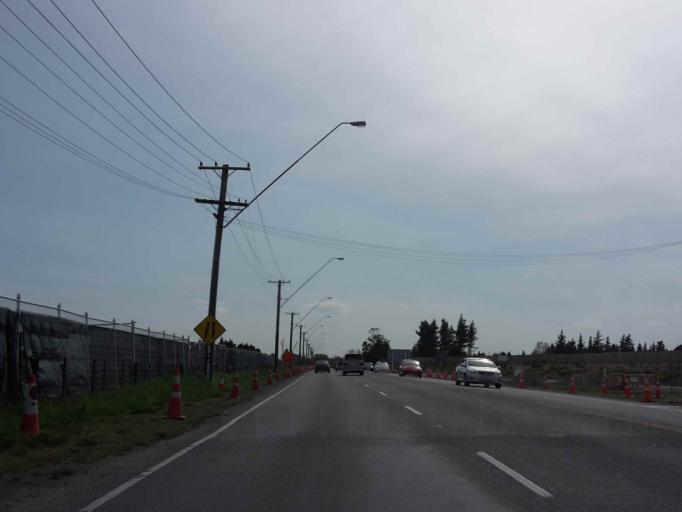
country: NZ
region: Canterbury
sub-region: Christchurch City
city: Christchurch
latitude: -43.4918
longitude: 172.5505
